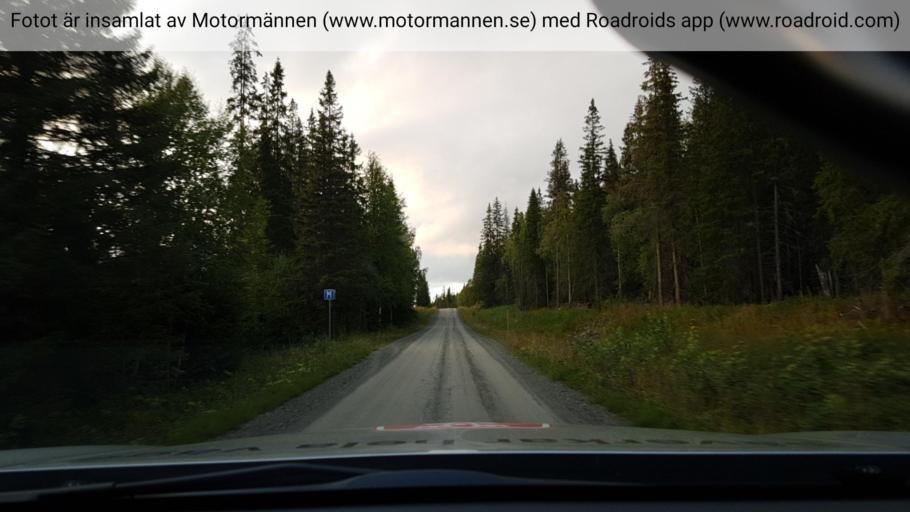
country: SE
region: Vaesterbotten
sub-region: Vilhelmina Kommun
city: Sjoberg
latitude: 65.5821
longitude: 15.2982
